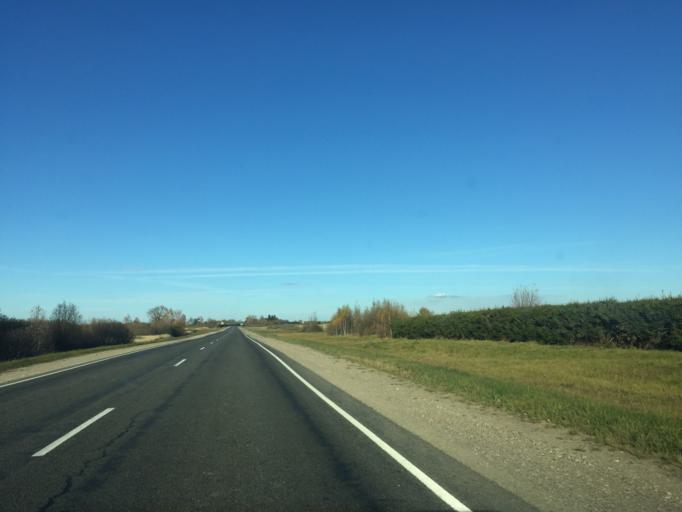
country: BY
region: Vitebsk
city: Dzisna
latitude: 55.3290
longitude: 28.2793
